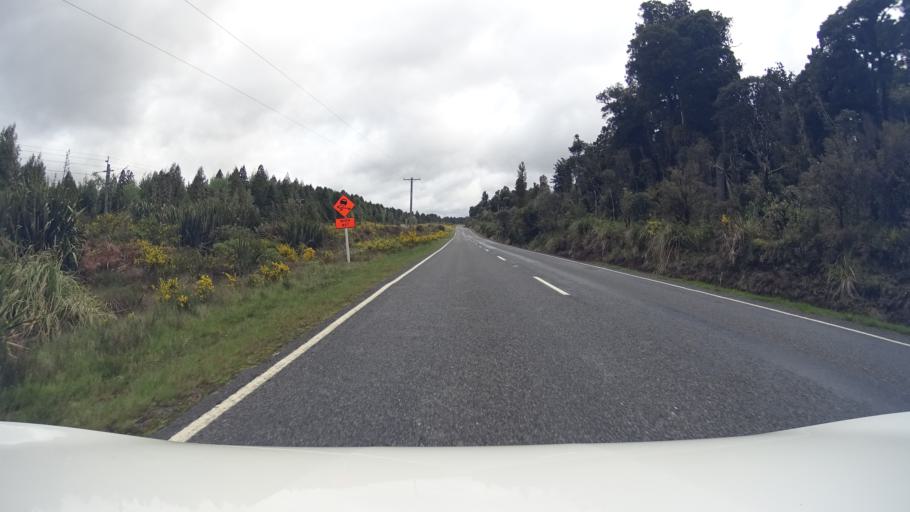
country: NZ
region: Manawatu-Wanganui
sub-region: Ruapehu District
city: Waiouru
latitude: -39.2531
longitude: 175.3880
